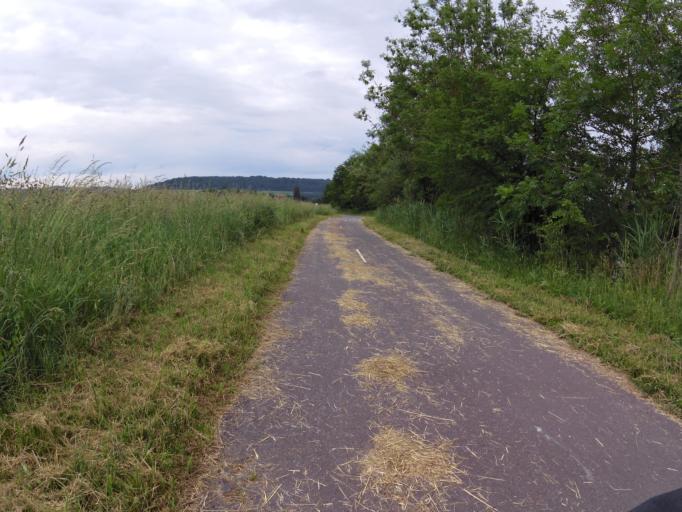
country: FR
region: Champagne-Ardenne
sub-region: Departement des Ardennes
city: Dom-le-Mesnil
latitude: 49.6969
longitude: 4.8355
